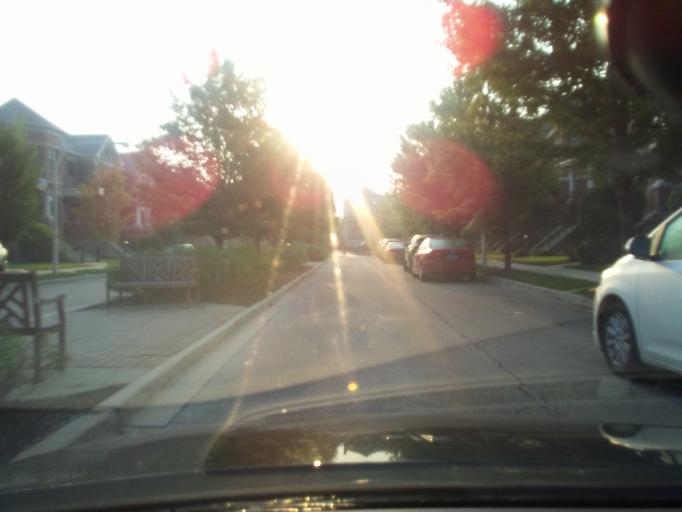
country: US
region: Illinois
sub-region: Cook County
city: Lincolnwood
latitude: 41.9476
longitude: -87.6917
